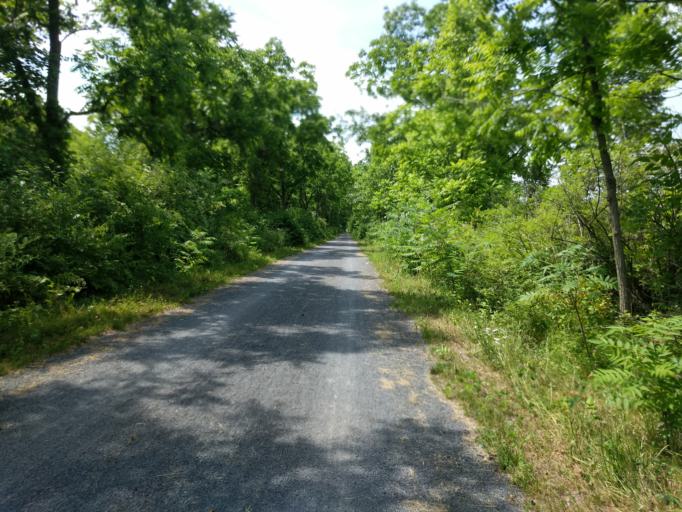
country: US
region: New York
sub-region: Tompkins County
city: Northwest Ithaca
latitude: 42.5225
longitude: -76.5816
